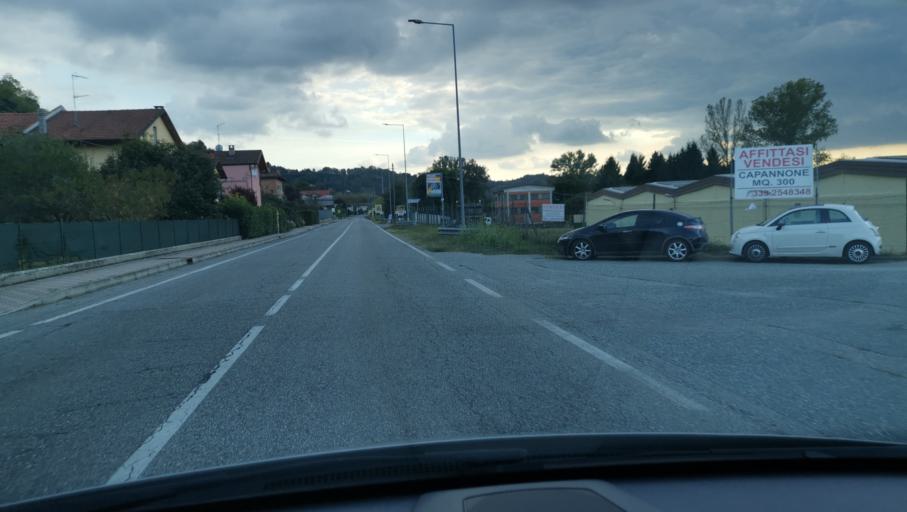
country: IT
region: Piedmont
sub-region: Provincia di Torino
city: Piana San Raffaele
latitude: 45.1571
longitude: 7.8525
